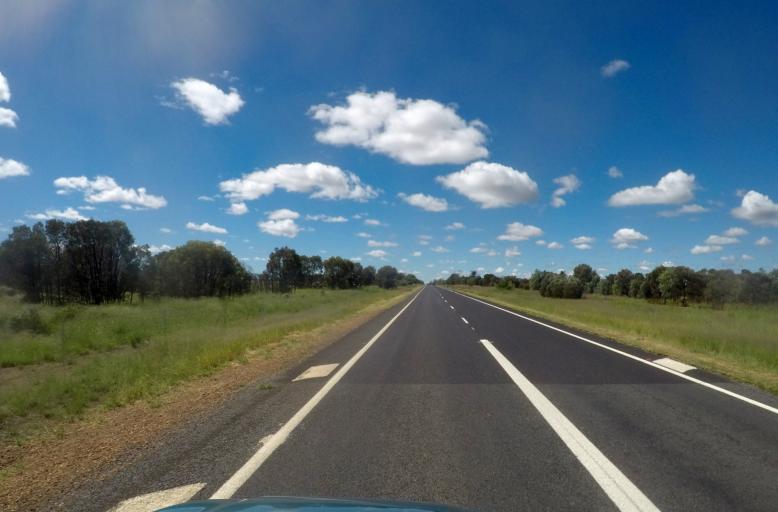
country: AU
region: Queensland
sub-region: Western Downs
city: Westcourt
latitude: -26.6417
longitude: 149.9904
